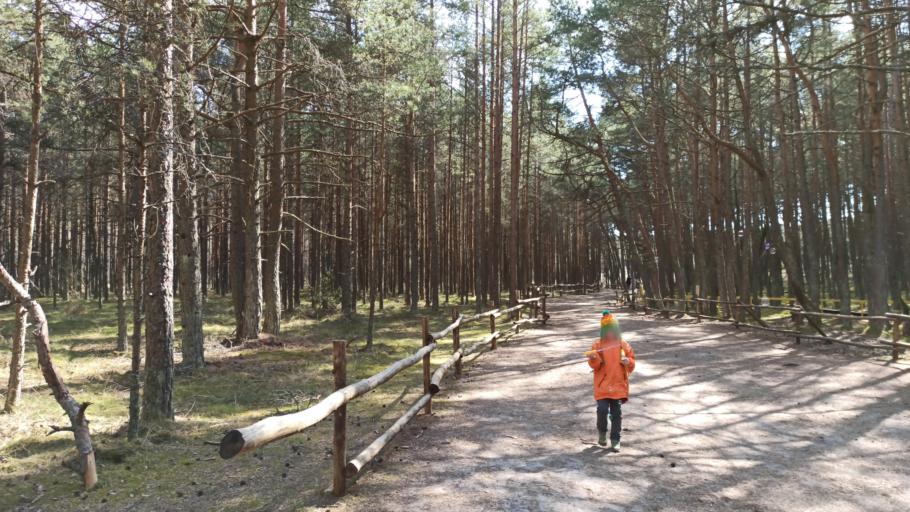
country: LT
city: Nida
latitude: 55.1804
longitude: 20.8633
